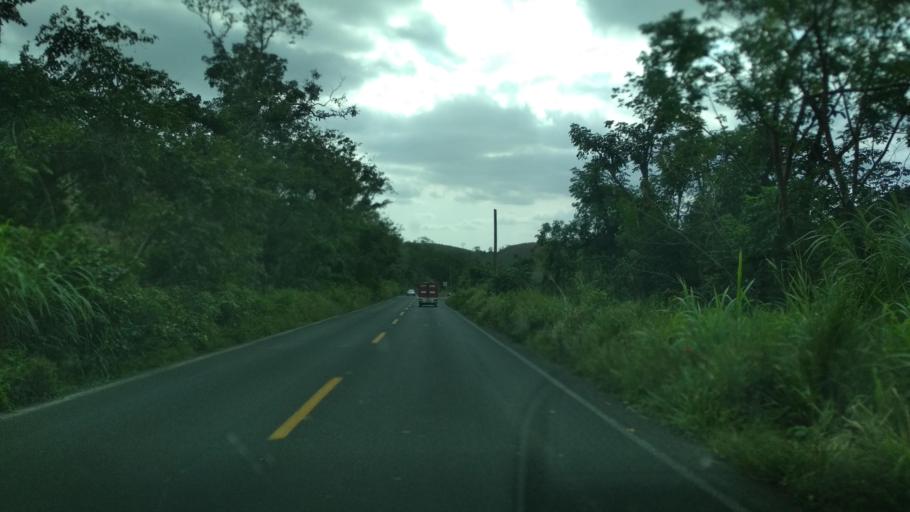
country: MX
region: Veracruz
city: Papantla de Olarte
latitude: 20.4652
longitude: -97.2658
